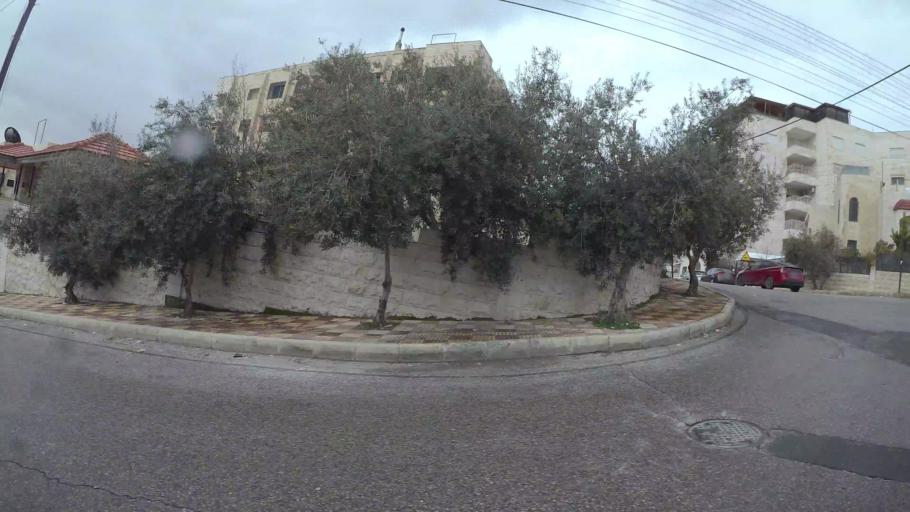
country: JO
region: Amman
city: Al Jubayhah
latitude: 31.9875
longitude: 35.8605
